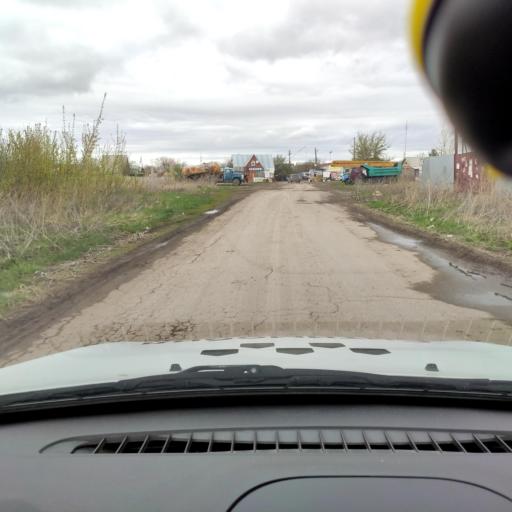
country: RU
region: Samara
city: Tol'yatti
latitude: 53.5806
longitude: 49.3142
